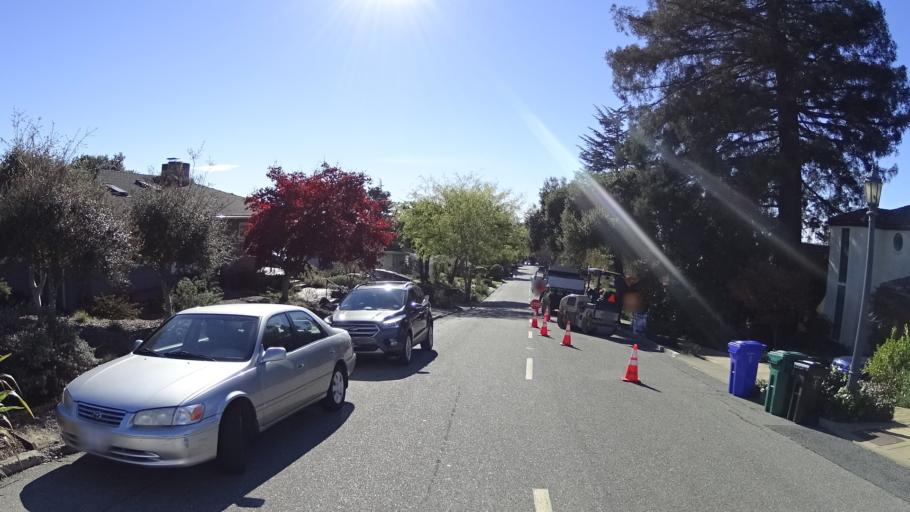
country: US
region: California
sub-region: Alameda County
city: Piedmont
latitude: 37.8188
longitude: -122.2118
